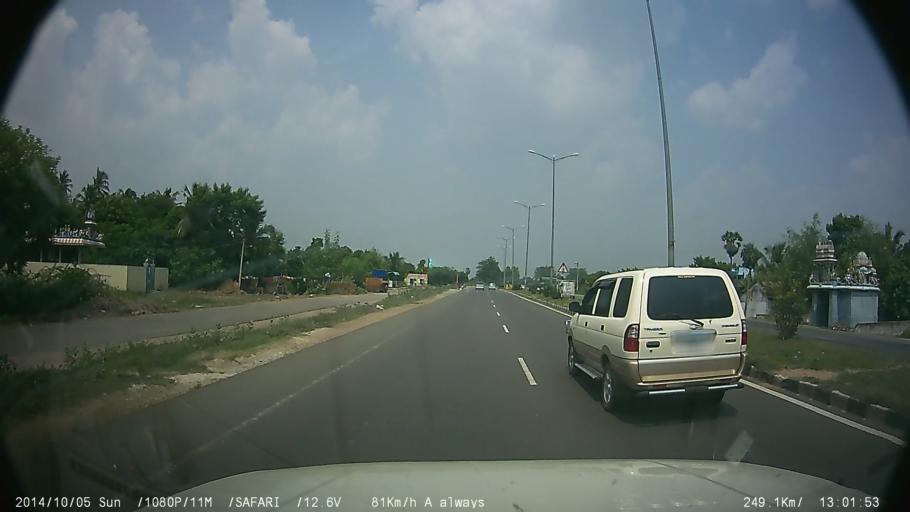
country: IN
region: Tamil Nadu
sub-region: Villupuram
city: Villupuram
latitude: 11.8400
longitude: 79.4306
